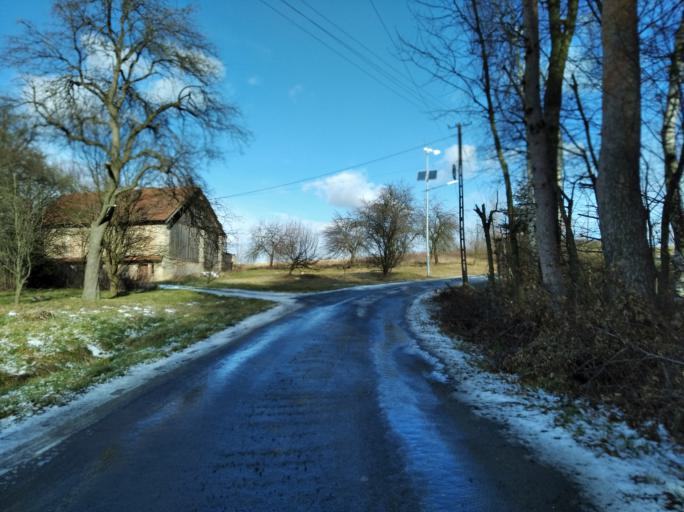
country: PL
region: Subcarpathian Voivodeship
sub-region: Powiat strzyzowski
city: Strzyzow
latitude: 49.9005
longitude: 21.7653
